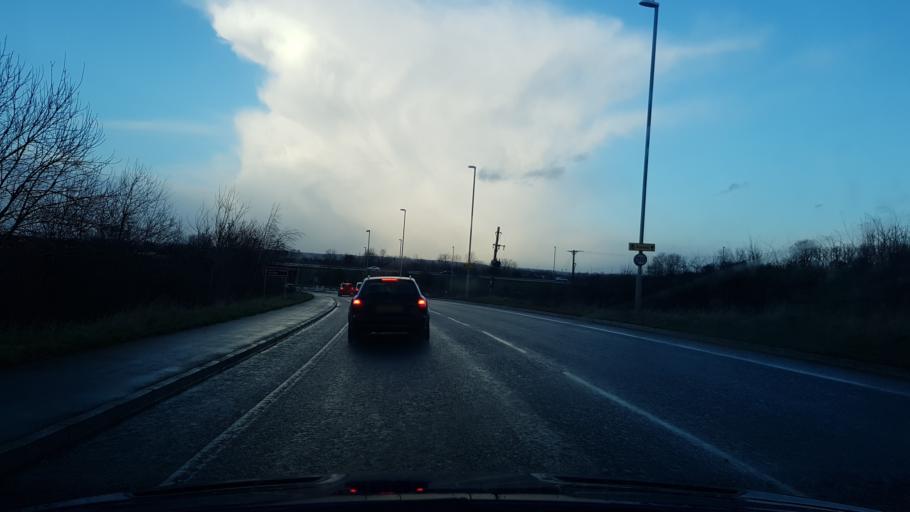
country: GB
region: England
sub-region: City and Borough of Wakefield
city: Castleford
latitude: 53.7046
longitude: -1.3687
